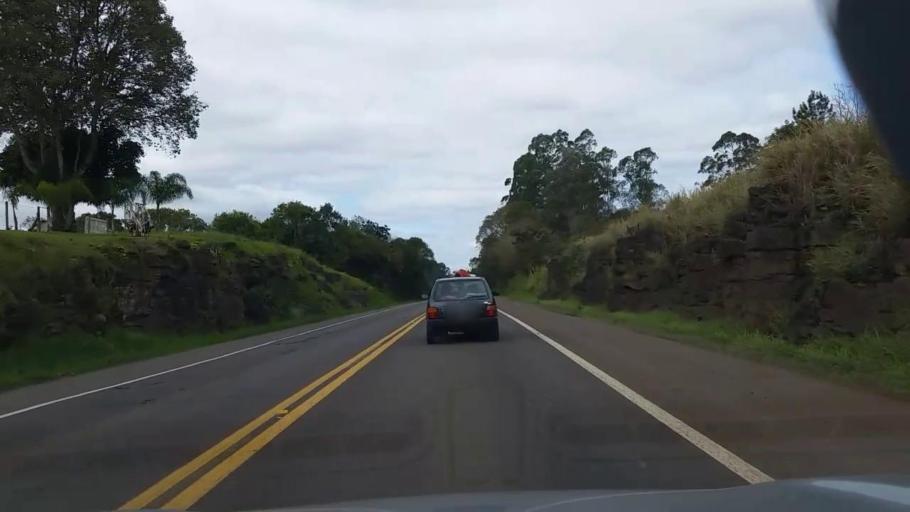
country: BR
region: Rio Grande do Sul
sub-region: Arroio Do Meio
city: Arroio do Meio
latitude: -29.4074
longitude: -52.0324
